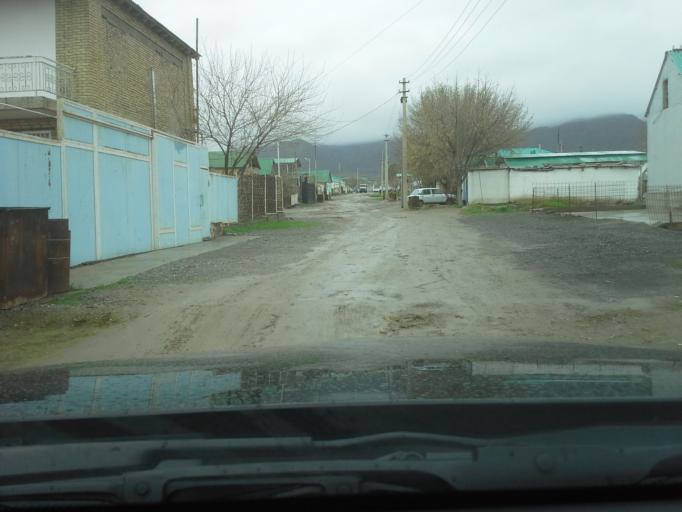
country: TM
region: Ahal
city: Abadan
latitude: 37.9672
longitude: 58.2099
